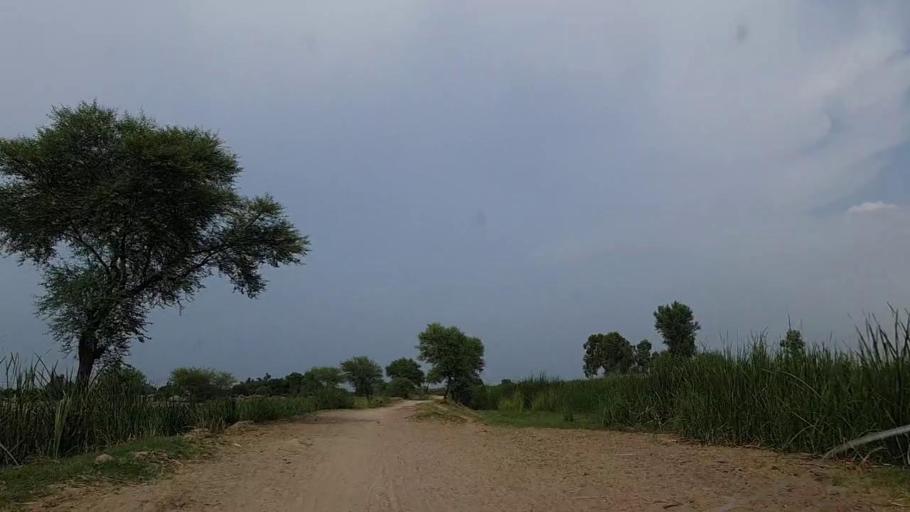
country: PK
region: Sindh
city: Khanpur
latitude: 27.8181
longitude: 69.5359
